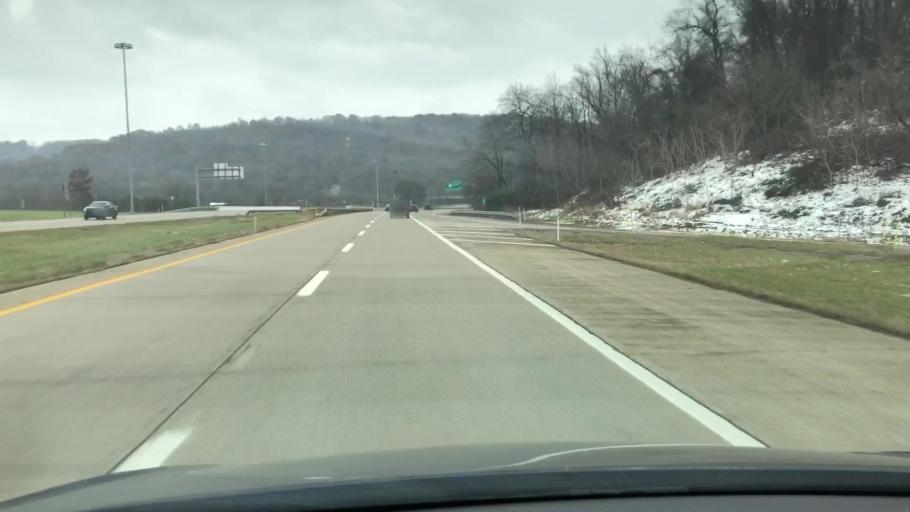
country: US
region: Pennsylvania
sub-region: Westmoreland County
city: New Stanton
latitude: 40.2271
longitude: -79.5953
